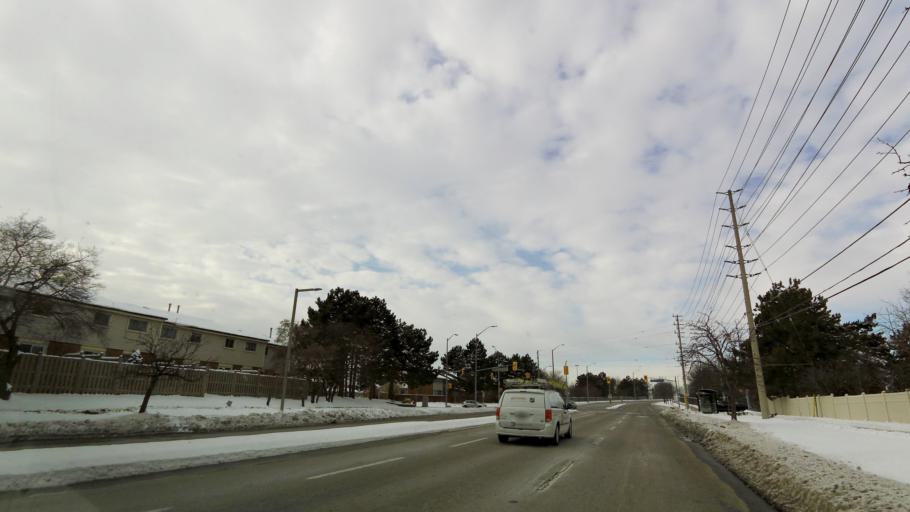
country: CA
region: Ontario
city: Mississauga
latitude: 43.5470
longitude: -79.6985
